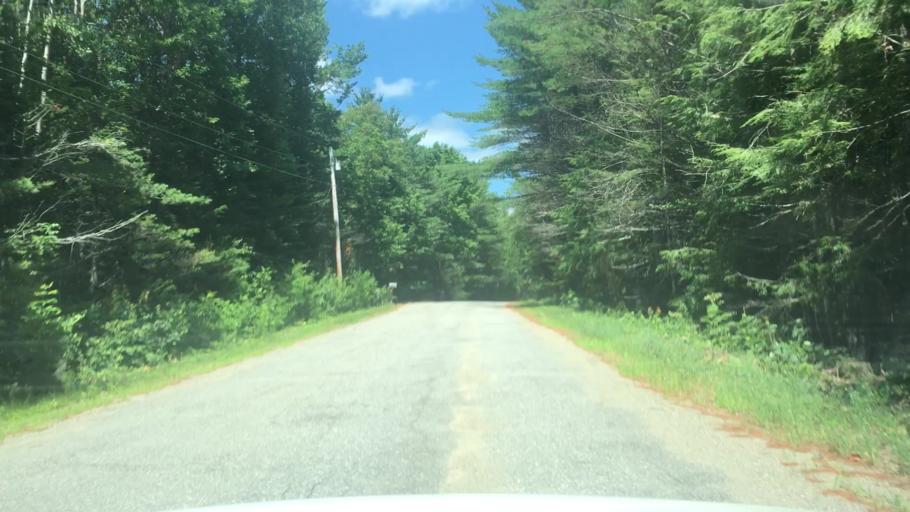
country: US
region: Maine
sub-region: Waldo County
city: Searsmont
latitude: 44.4540
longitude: -69.3137
